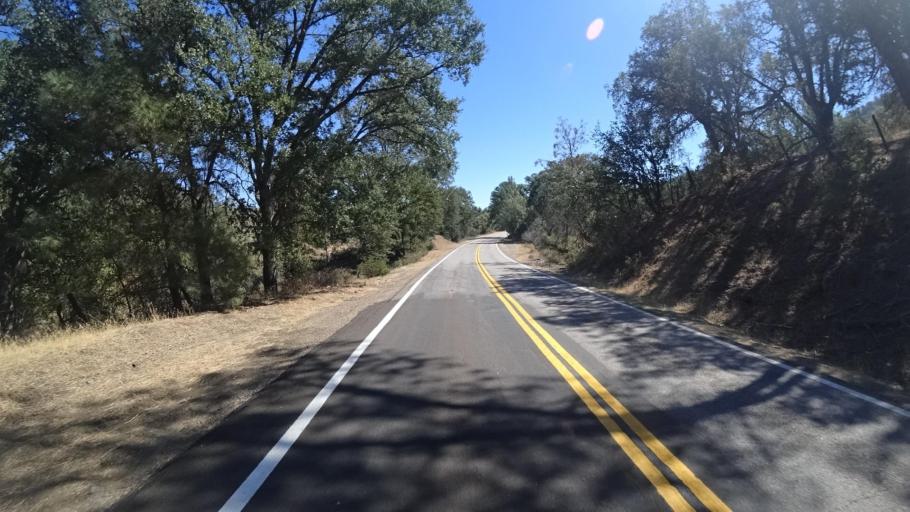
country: US
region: California
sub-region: Fresno County
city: Coalinga
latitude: 36.2011
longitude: -120.7274
